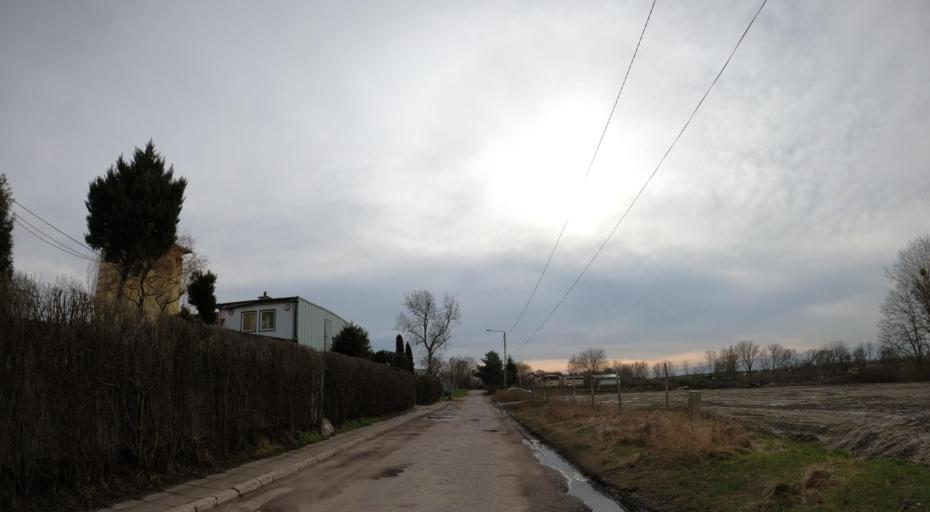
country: PL
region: West Pomeranian Voivodeship
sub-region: Powiat pyrzycki
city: Pyrzyce
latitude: 53.1342
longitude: 14.9079
